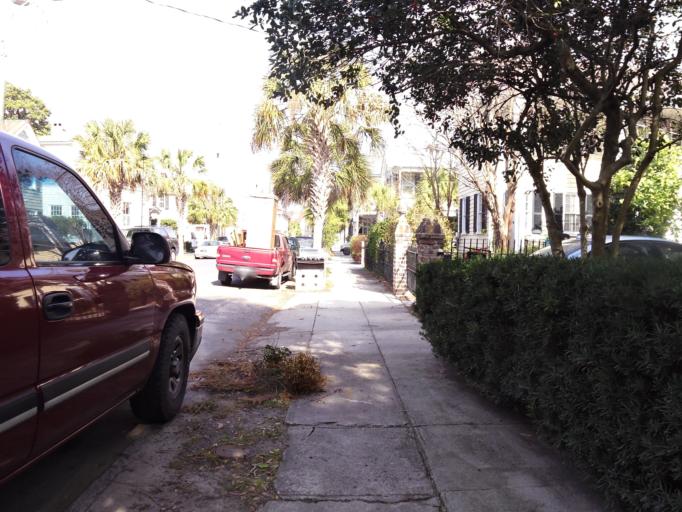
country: US
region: South Carolina
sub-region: Charleston County
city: Charleston
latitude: 32.7731
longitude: -79.9380
